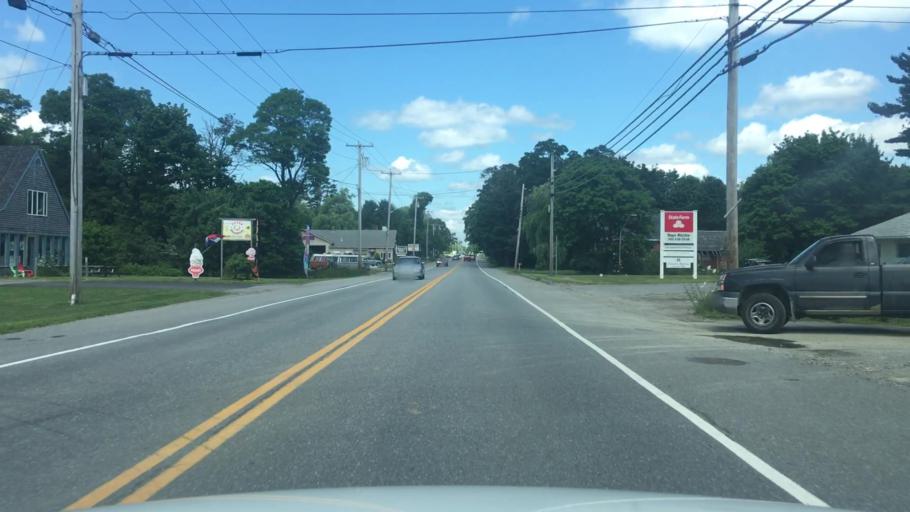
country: US
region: Maine
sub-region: Waldo County
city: Belfast
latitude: 44.4025
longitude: -68.9891
